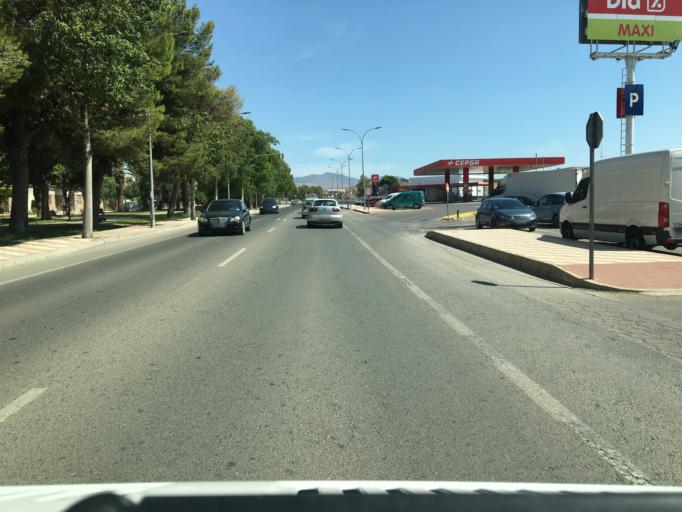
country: ES
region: Andalusia
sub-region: Provincia de Almeria
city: Huercal-Overa
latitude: 37.4005
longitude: -1.9390
